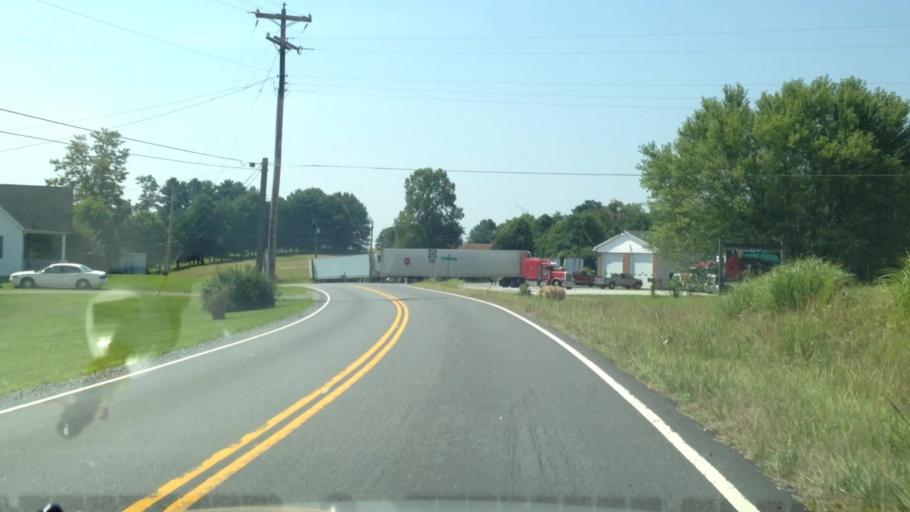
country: US
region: Virginia
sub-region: Patrick County
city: Stuart
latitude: 36.5828
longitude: -80.2782
